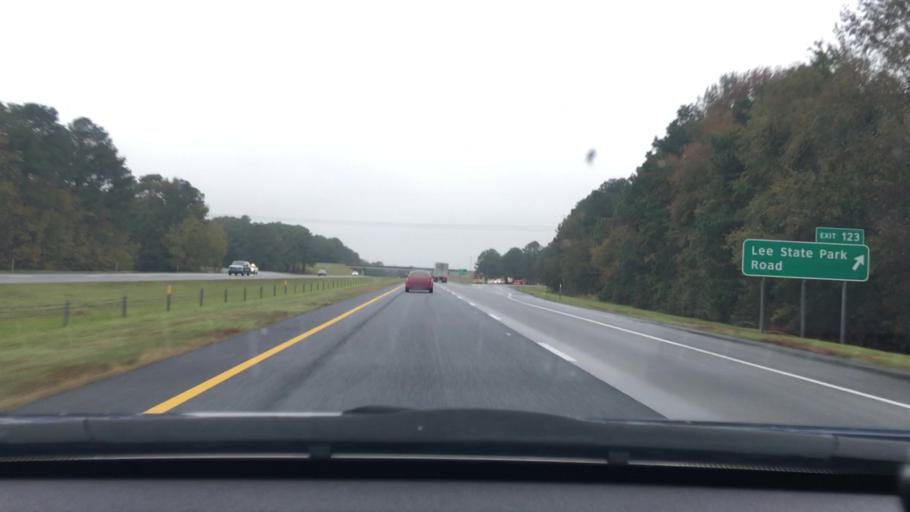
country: US
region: South Carolina
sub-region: Lee County
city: Bishopville
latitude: 34.1910
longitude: -80.1599
